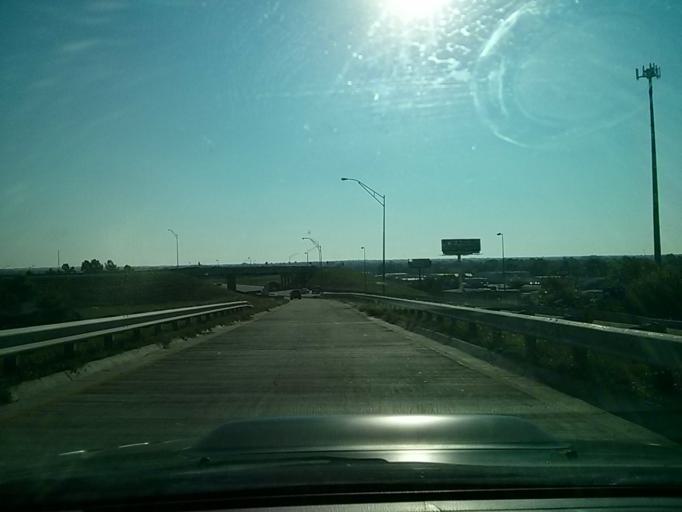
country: US
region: Oklahoma
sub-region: Tulsa County
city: Tulsa
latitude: 36.1622
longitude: -95.8839
